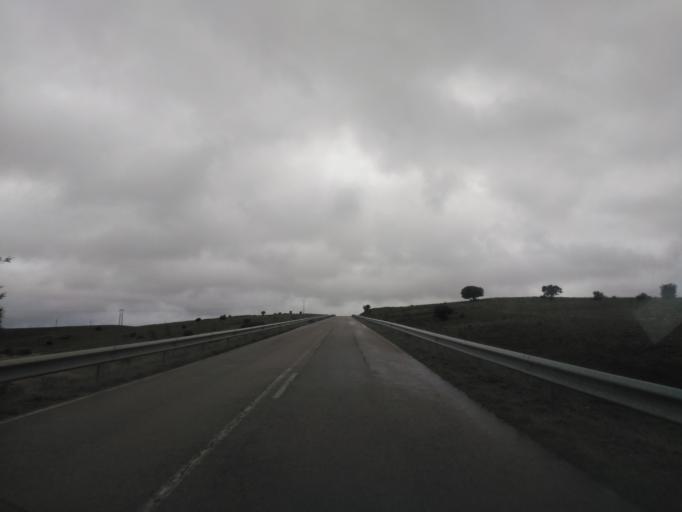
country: ES
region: Castille and Leon
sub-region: Provincia de Salamanca
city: Doninos de Salamanca
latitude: 40.9706
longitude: -5.7138
